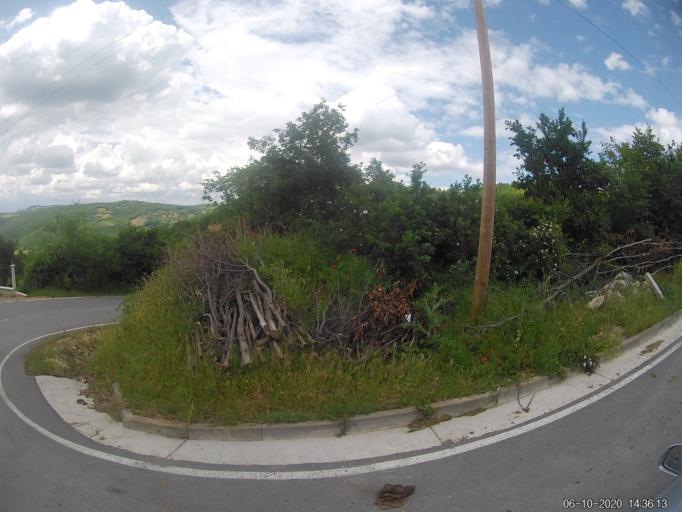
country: XK
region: Prizren
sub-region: Komuna e Therandes
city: Budakovo
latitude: 42.4111
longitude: 20.9366
